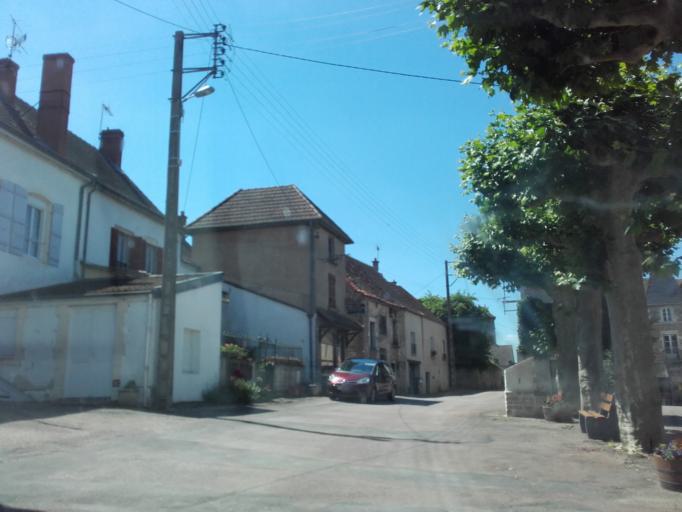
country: FR
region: Bourgogne
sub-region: Departement de Saone-et-Loire
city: Saint-Leger-sur-Dheune
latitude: 46.8954
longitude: 4.6693
